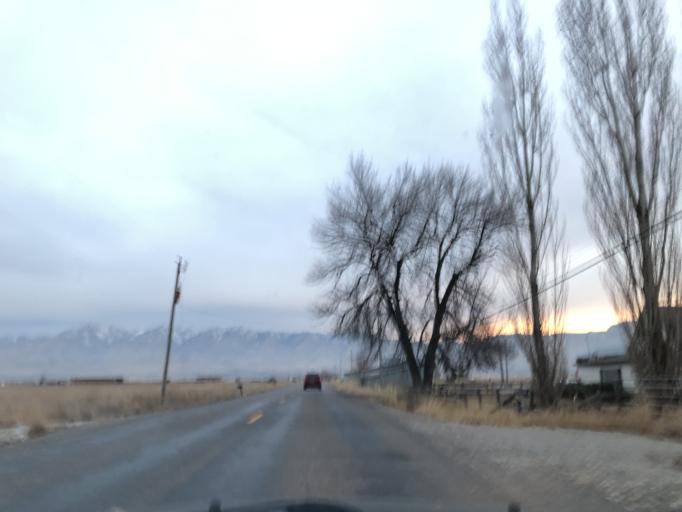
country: US
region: Utah
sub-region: Cache County
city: Benson
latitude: 41.7947
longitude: -111.9011
